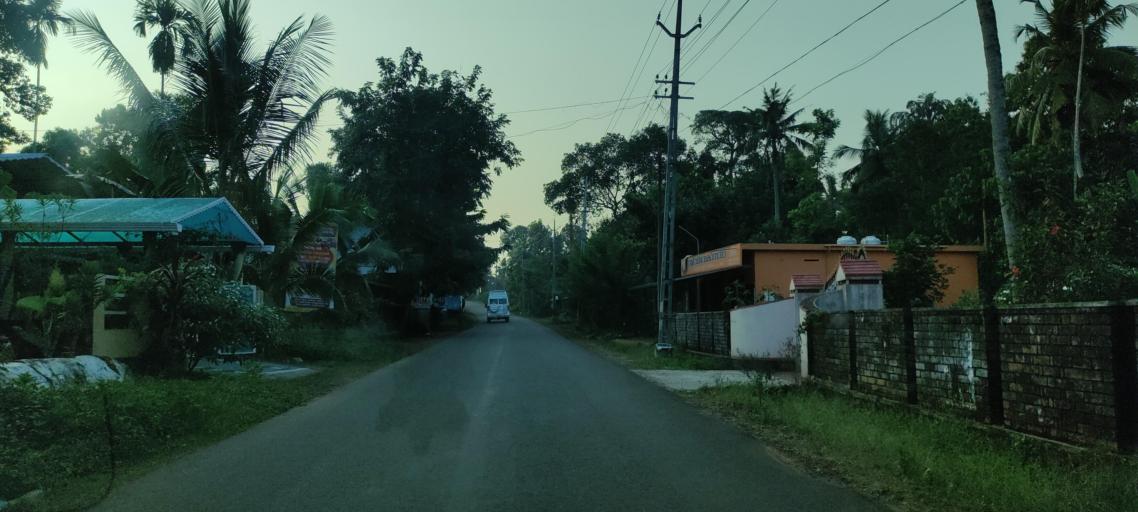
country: IN
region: Kerala
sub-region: Alappuzha
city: Kattanam
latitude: 9.1504
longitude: 76.5823
